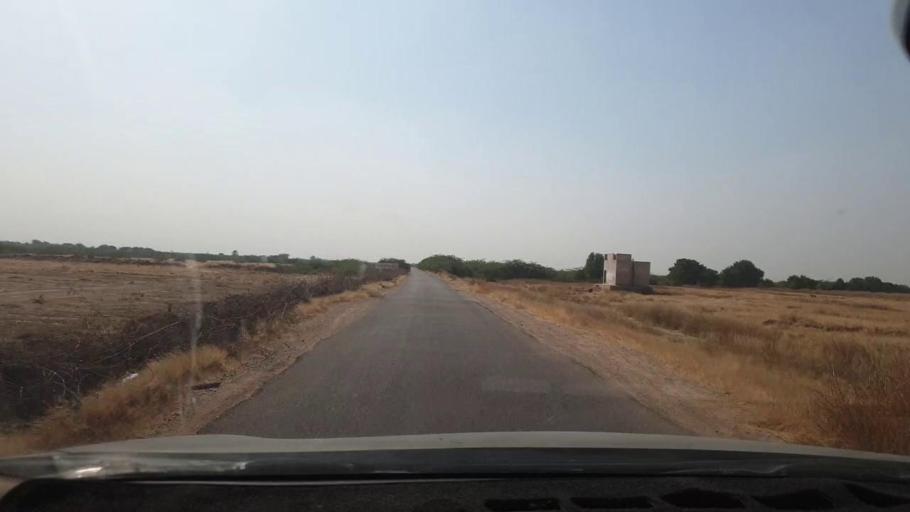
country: PK
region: Sindh
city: Malir Cantonment
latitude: 25.1064
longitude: 67.2004
